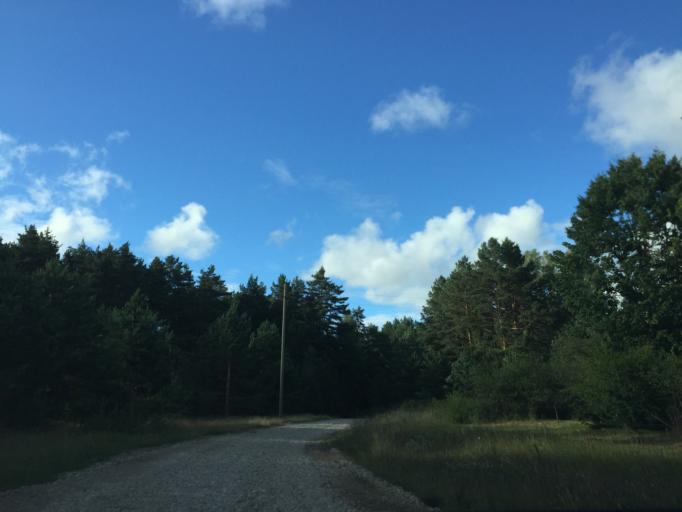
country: LV
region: Adazi
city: Adazi
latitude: 57.1316
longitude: 24.3457
